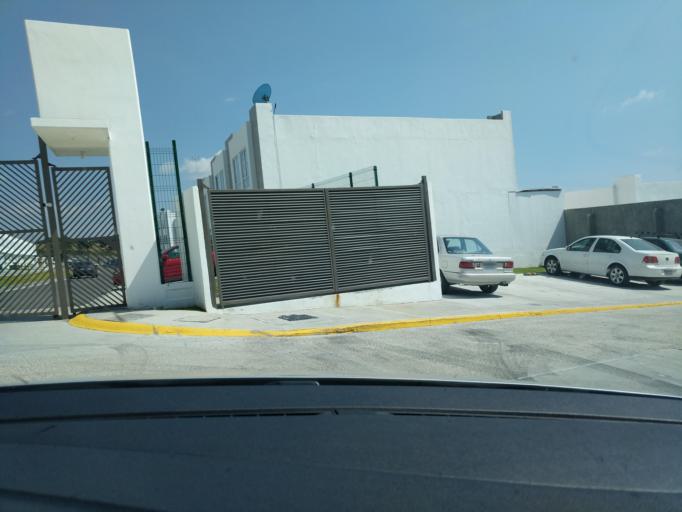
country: MX
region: Puebla
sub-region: Puebla
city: Galaxia la Calera
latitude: 19.0065
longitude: -98.1397
